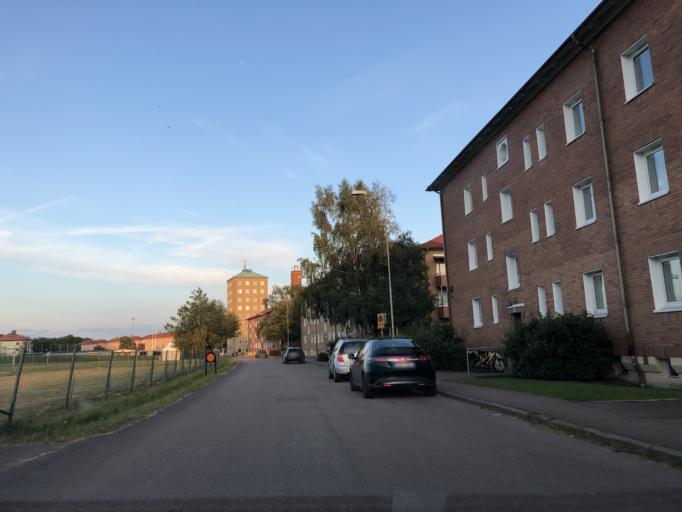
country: SE
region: Vaestra Goetaland
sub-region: Goteborg
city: Majorna
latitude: 57.7308
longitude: 11.9235
